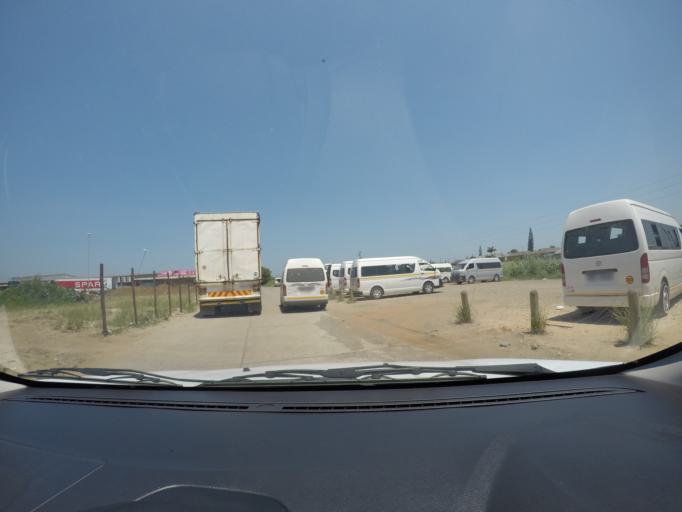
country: ZA
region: KwaZulu-Natal
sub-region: uThungulu District Municipality
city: eSikhawini
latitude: -28.8730
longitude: 31.8984
